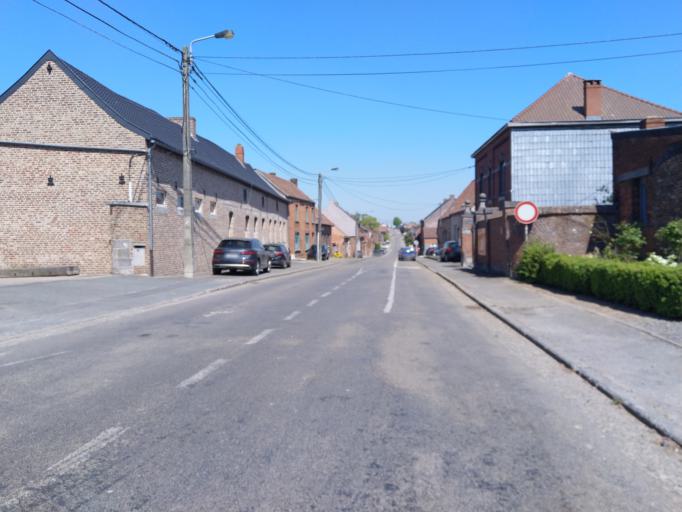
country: BE
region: Wallonia
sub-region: Province du Hainaut
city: Soignies
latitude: 50.5929
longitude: 3.9985
